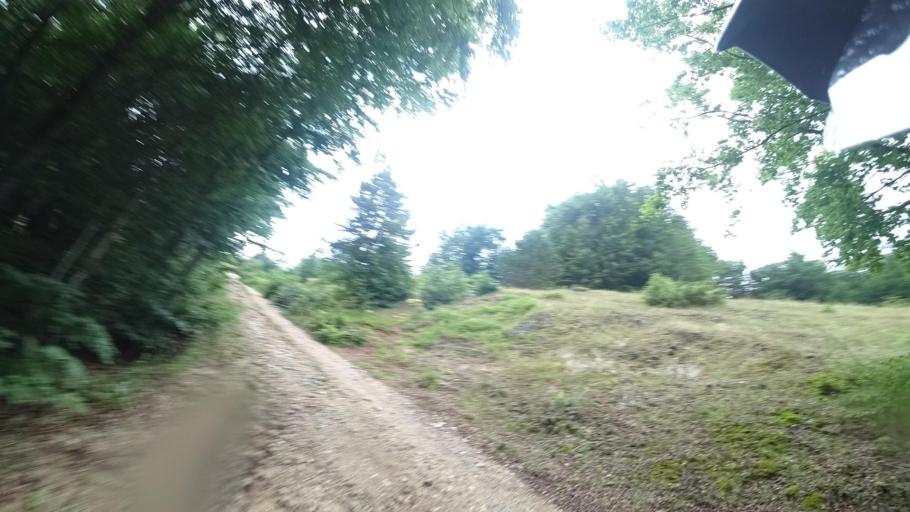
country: HR
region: Licko-Senjska
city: Jezerce
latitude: 44.7419
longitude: 15.6295
